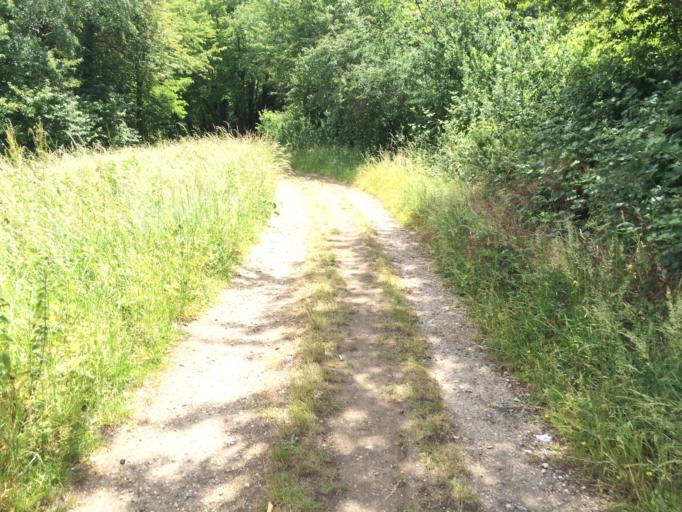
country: FR
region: Ile-de-France
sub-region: Departement de l'Essonne
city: Les Ulis
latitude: 48.6698
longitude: 2.1851
